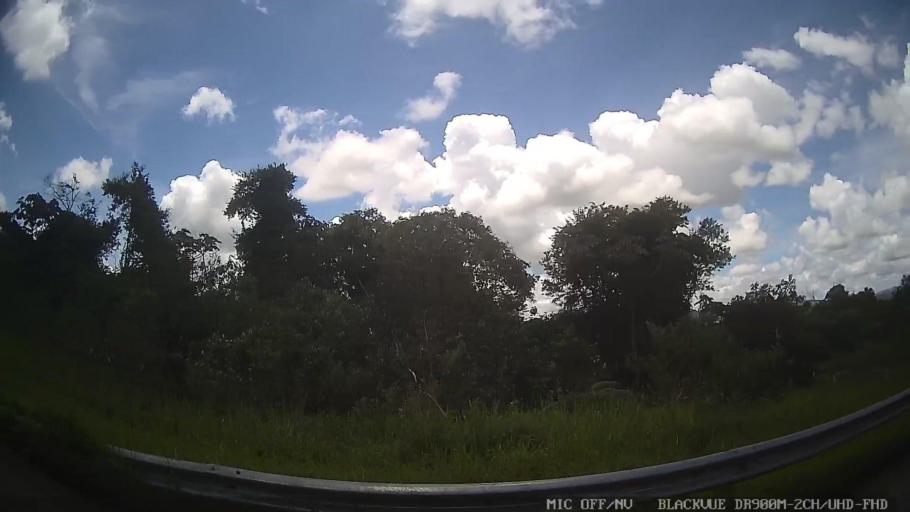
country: BR
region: Sao Paulo
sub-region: Amparo
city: Amparo
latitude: -22.7967
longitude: -46.7173
